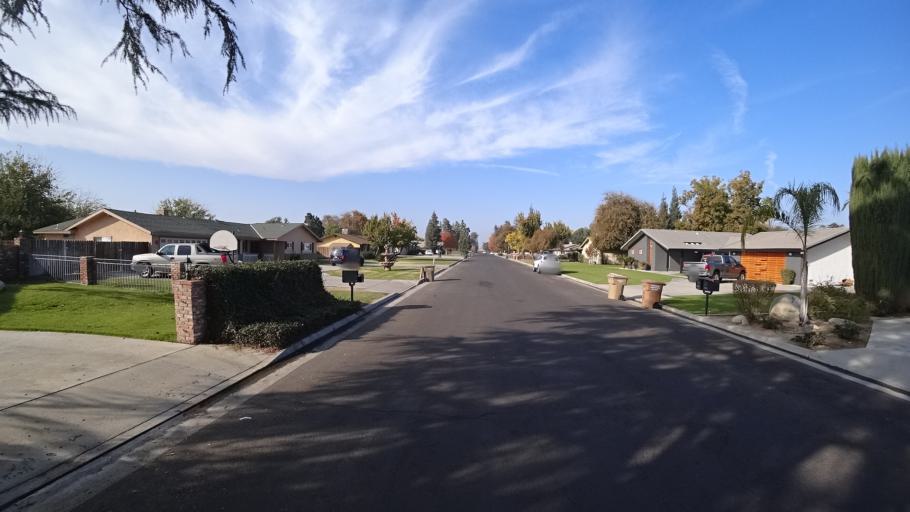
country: US
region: California
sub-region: Kern County
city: Rosedale
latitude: 35.3671
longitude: -119.1474
